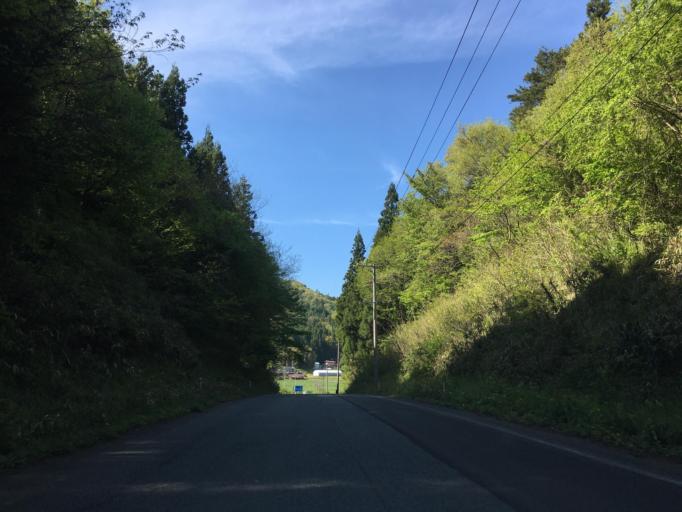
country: JP
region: Fukushima
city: Funehikimachi-funehiki
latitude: 37.3520
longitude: 140.6318
